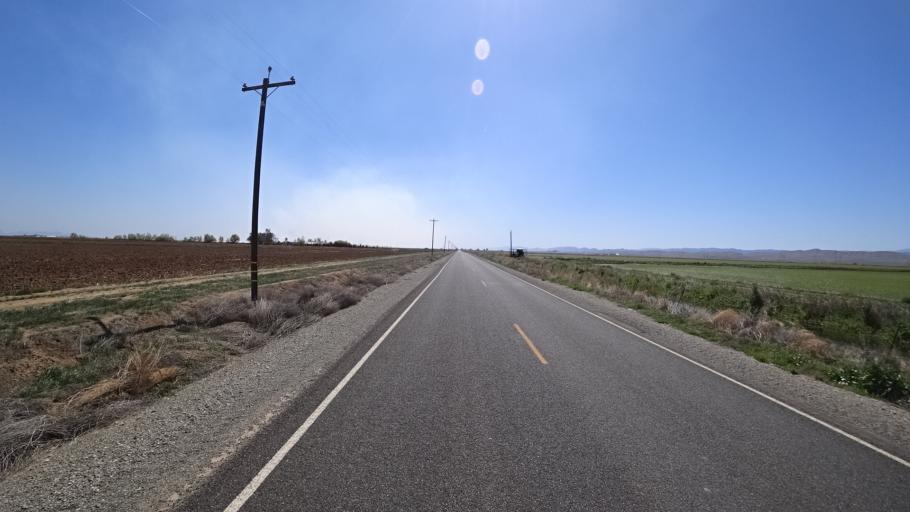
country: US
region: California
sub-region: Glenn County
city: Willows
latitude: 39.4335
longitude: -122.2485
